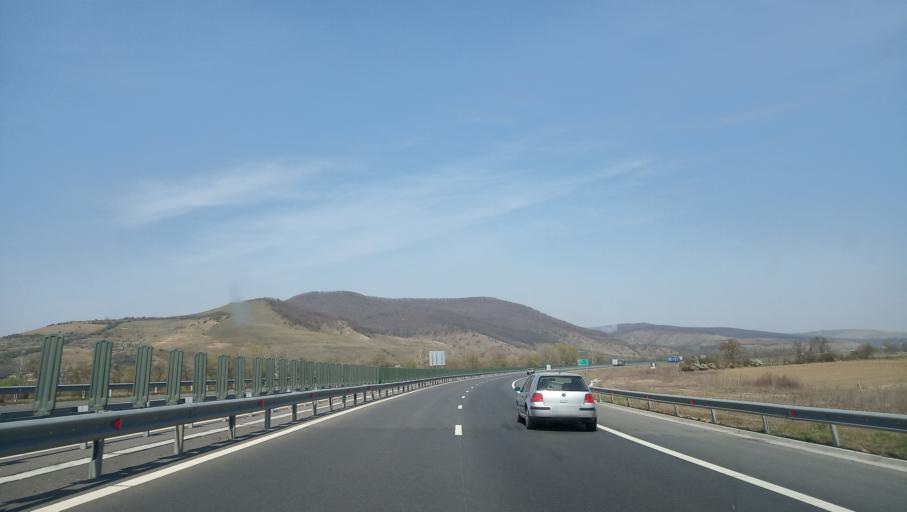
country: RO
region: Alba
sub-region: Comuna Miraslau
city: Miraslau
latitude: 46.3528
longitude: 23.7241
